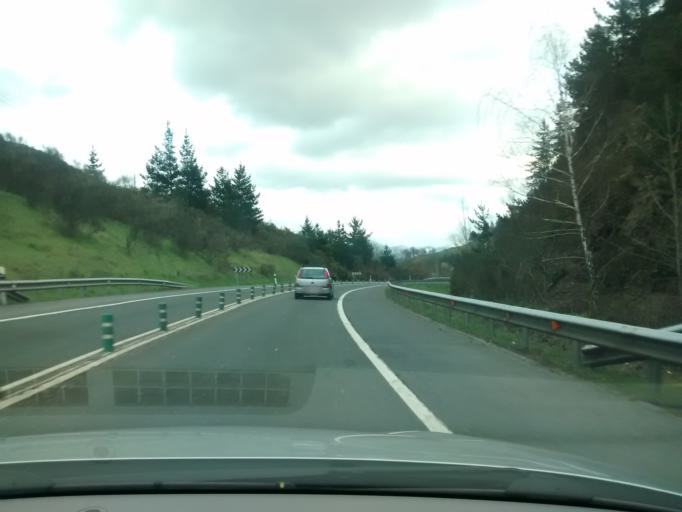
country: ES
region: Basque Country
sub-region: Bizkaia
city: Balmaseda
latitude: 43.2031
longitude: -3.1738
